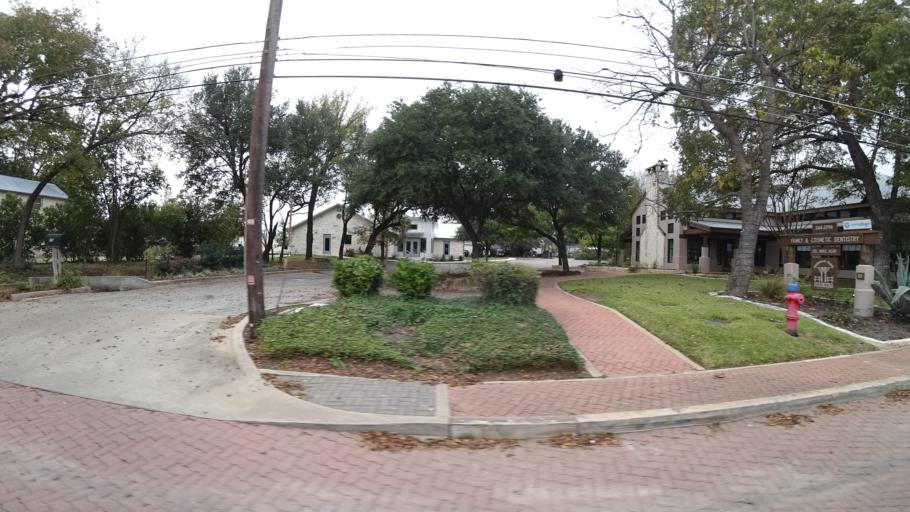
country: US
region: Texas
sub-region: Williamson County
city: Round Rock
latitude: 30.5166
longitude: -97.6904
